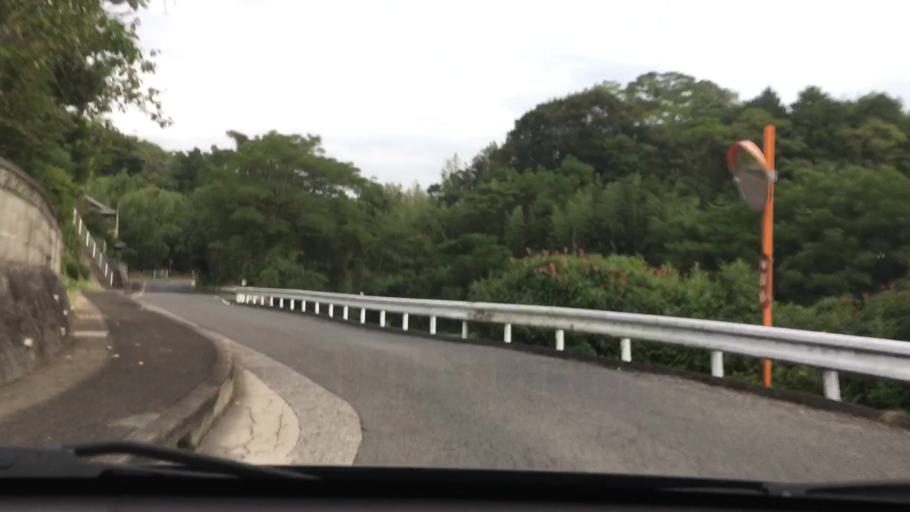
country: JP
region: Nagasaki
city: Sasebo
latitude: 33.0049
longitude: 129.7631
